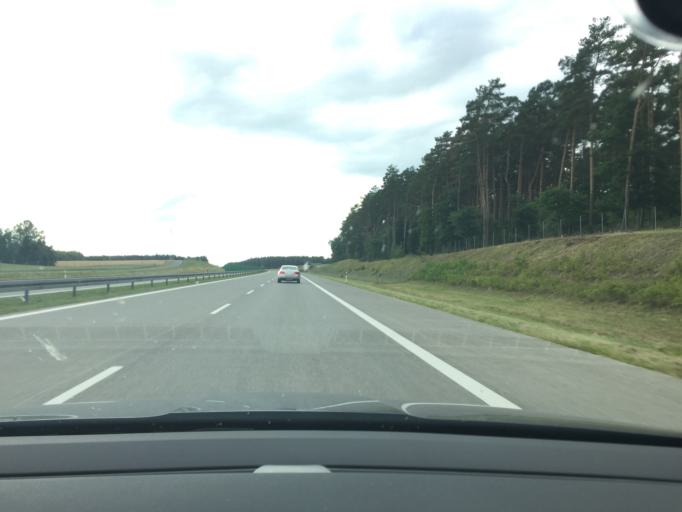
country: PL
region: Lubusz
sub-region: Powiat swiebodzinski
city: Lubrza
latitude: 52.3184
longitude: 15.4192
